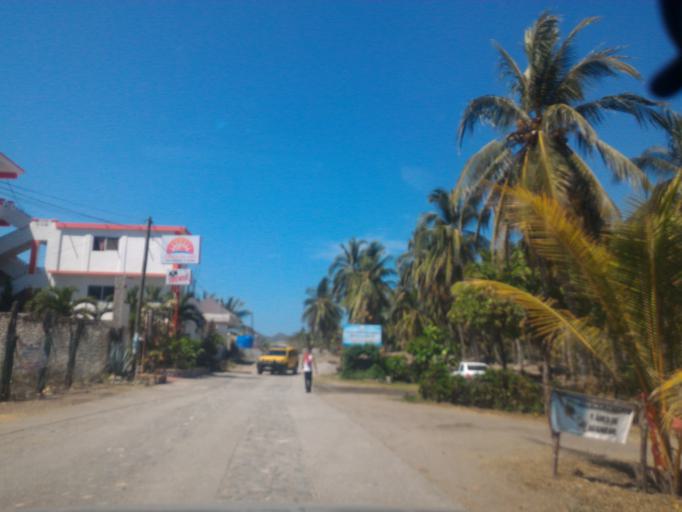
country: MX
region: Michoacan
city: Coahuayana Viejo
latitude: 18.5837
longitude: -103.6750
